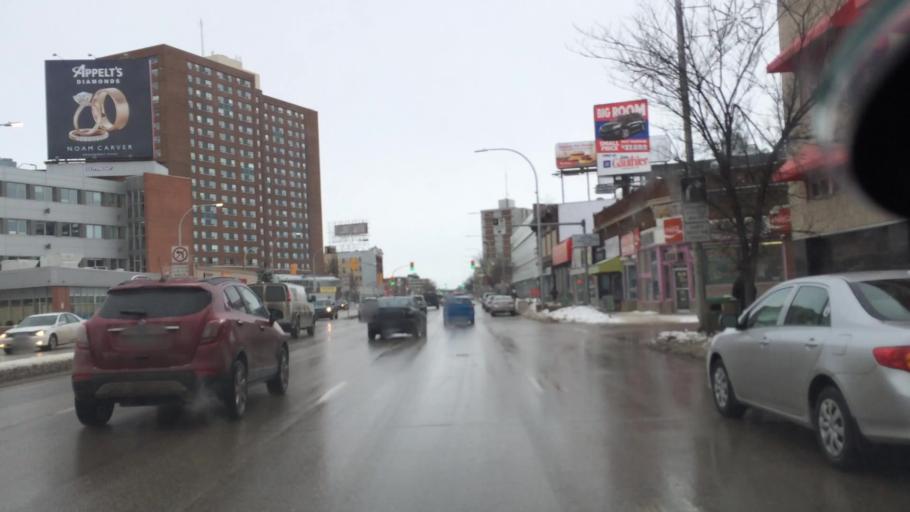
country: CA
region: Manitoba
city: Winnipeg
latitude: 49.8897
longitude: -97.1547
